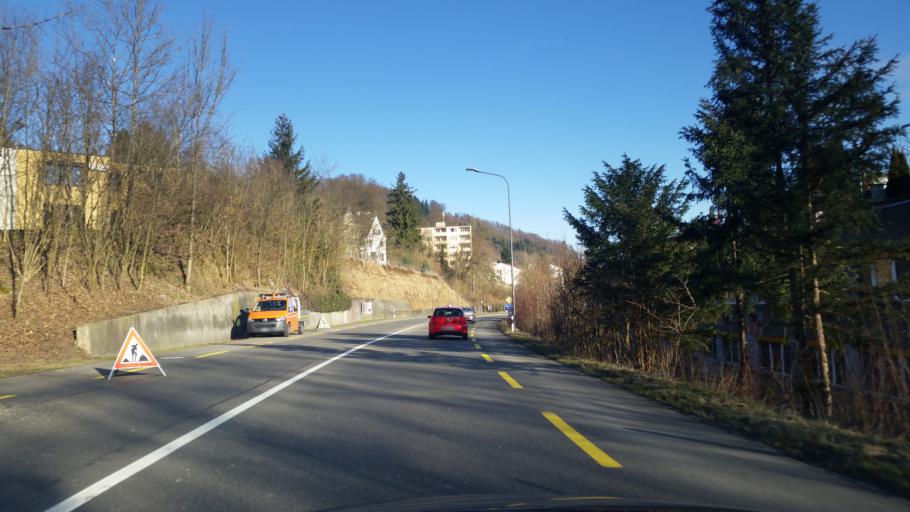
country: CH
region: Aargau
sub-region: Bezirk Baden
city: Wettingen
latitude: 47.4605
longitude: 8.3084
